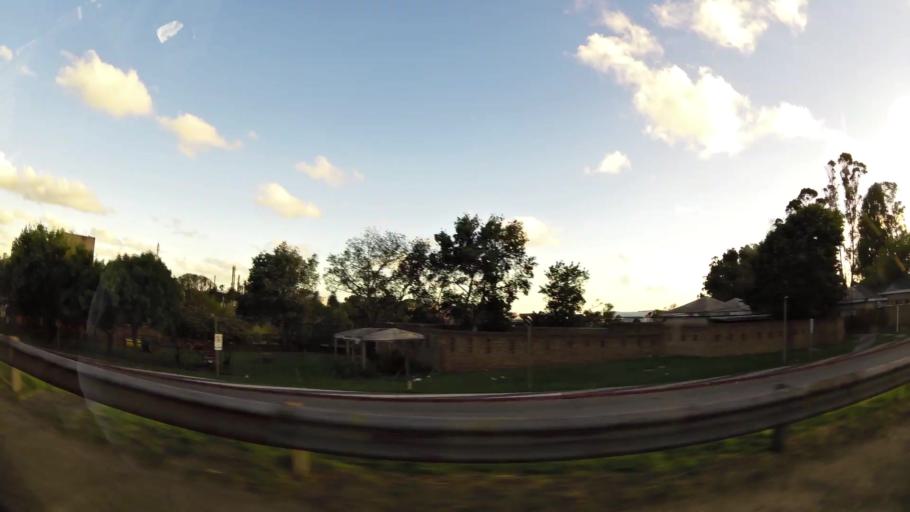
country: UY
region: Montevideo
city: Montevideo
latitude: -34.8724
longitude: -56.2332
